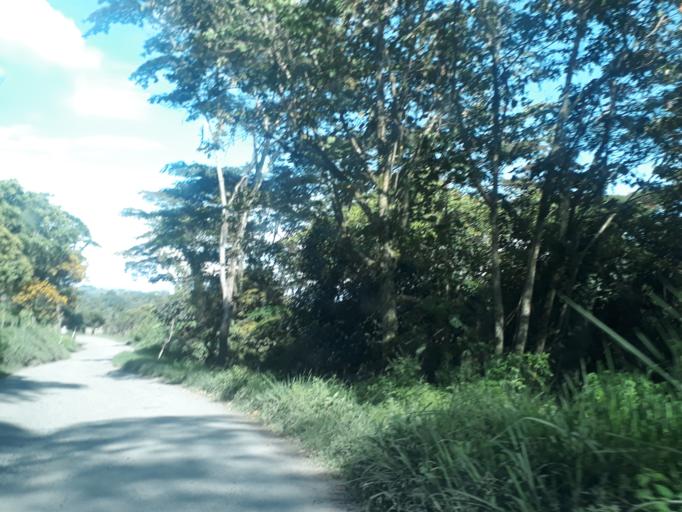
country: CO
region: Santander
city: Velez
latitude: 6.0537
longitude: -73.6479
